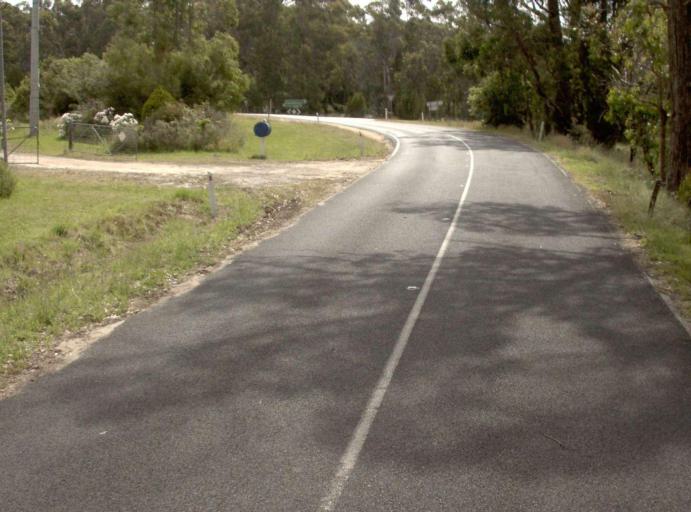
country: AU
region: Victoria
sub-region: Latrobe
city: Traralgon
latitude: -38.3811
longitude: 146.7601
